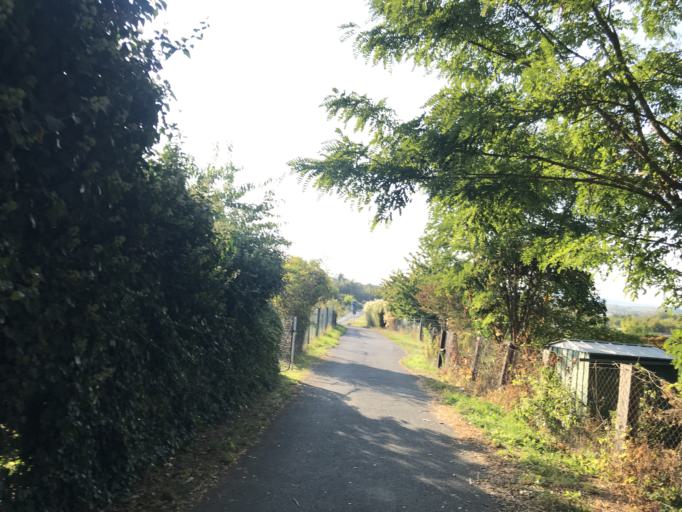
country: DE
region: Hesse
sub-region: Regierungsbezirk Kassel
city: Eschwege
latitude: 51.1913
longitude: 10.0334
